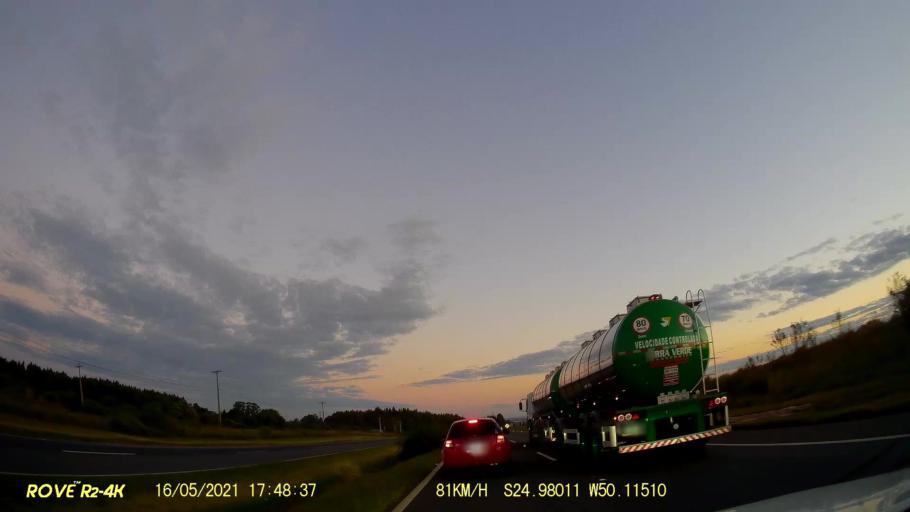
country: BR
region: Parana
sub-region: Carambei
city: Carambei
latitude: -24.9798
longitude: -50.1167
